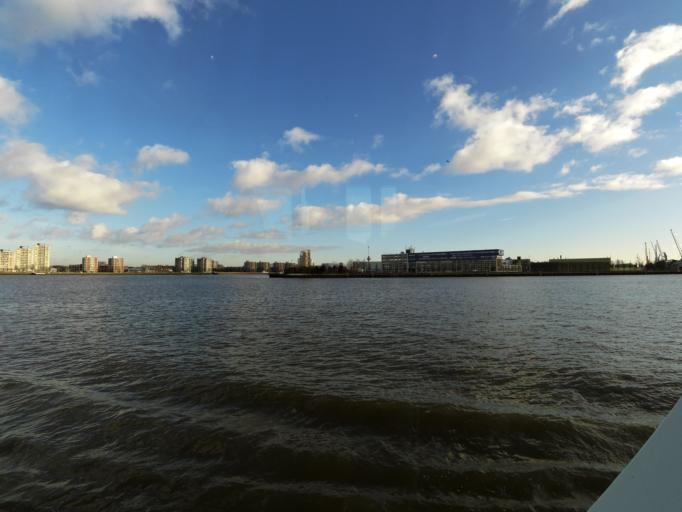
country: NL
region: South Holland
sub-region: Gemeente Rotterdam
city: Delfshaven
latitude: 51.8984
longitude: 4.4354
